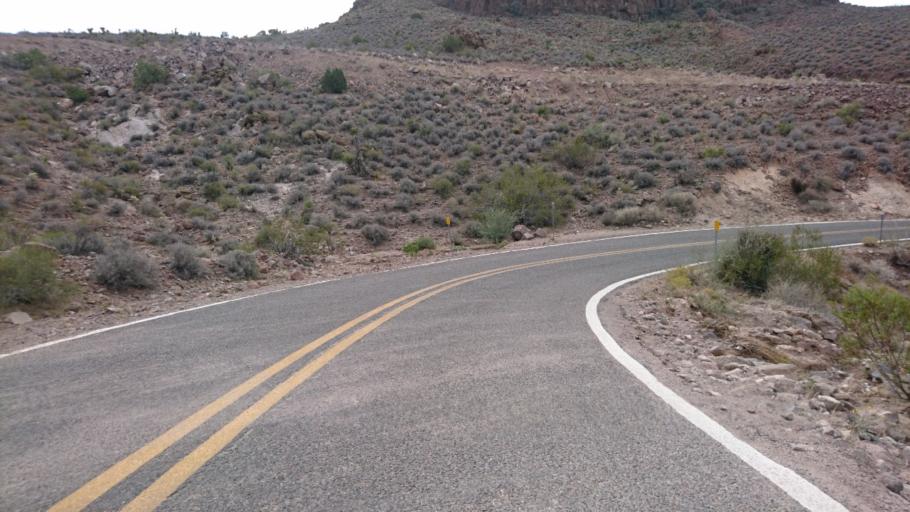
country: US
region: Arizona
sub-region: Mohave County
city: Golden Valley
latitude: 35.0460
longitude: -114.3623
